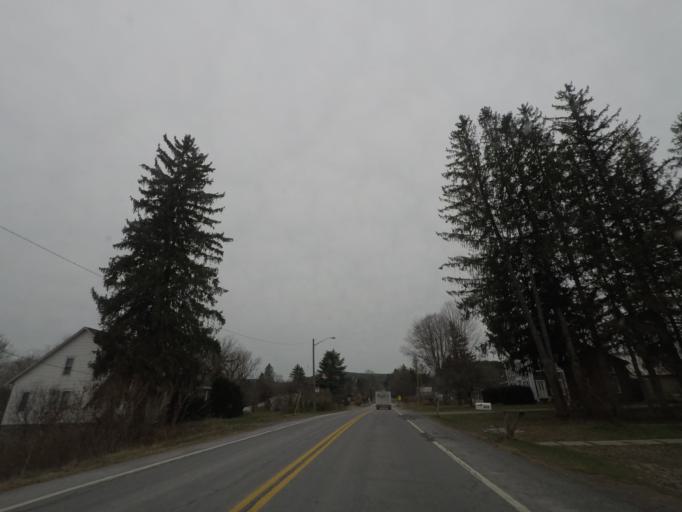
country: US
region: Massachusetts
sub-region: Berkshire County
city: Lanesborough
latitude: 42.5493
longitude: -73.3767
